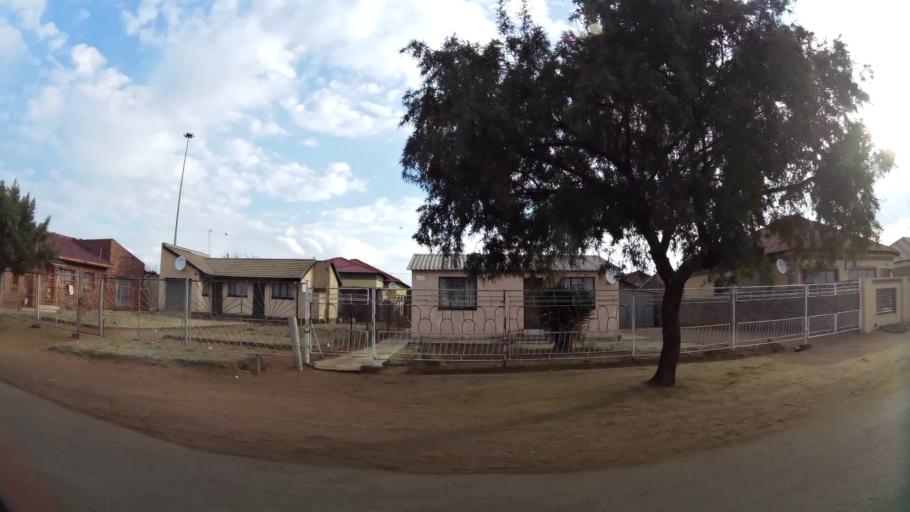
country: ZA
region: Gauteng
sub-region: Sedibeng District Municipality
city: Vanderbijlpark
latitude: -26.6823
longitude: 27.8720
